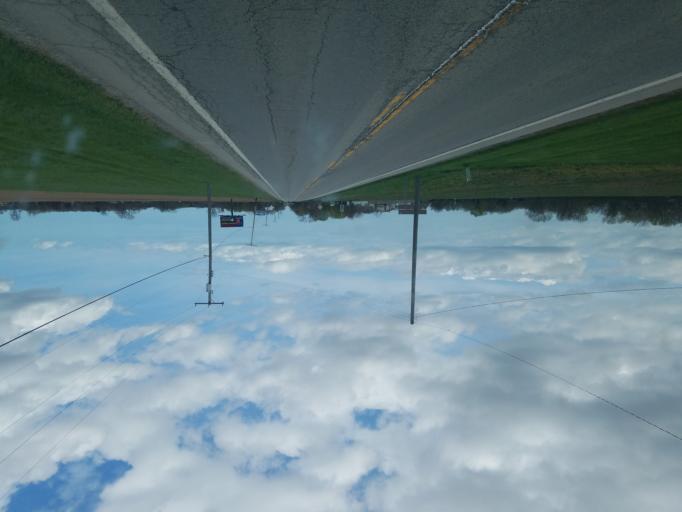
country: US
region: Ohio
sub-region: Erie County
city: Sandusky
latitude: 41.3527
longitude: -82.7534
